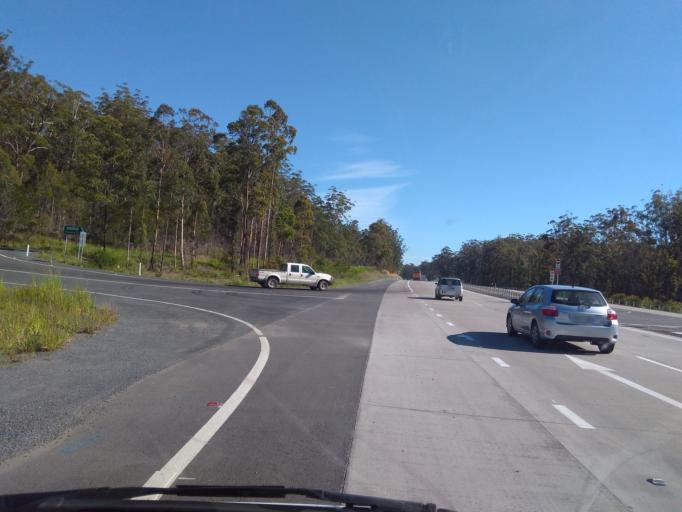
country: AU
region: New South Wales
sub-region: Kempsey
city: Kempsey
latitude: -31.1457
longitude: 152.8212
